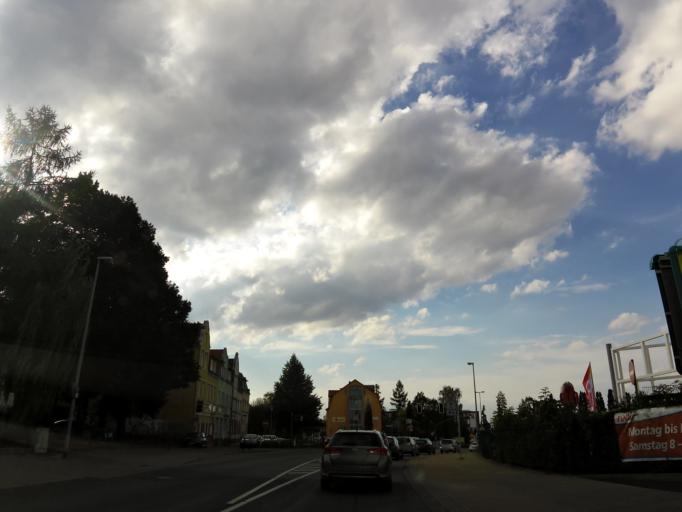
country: DE
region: Thuringia
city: Erfurt
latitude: 50.9706
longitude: 11.0576
